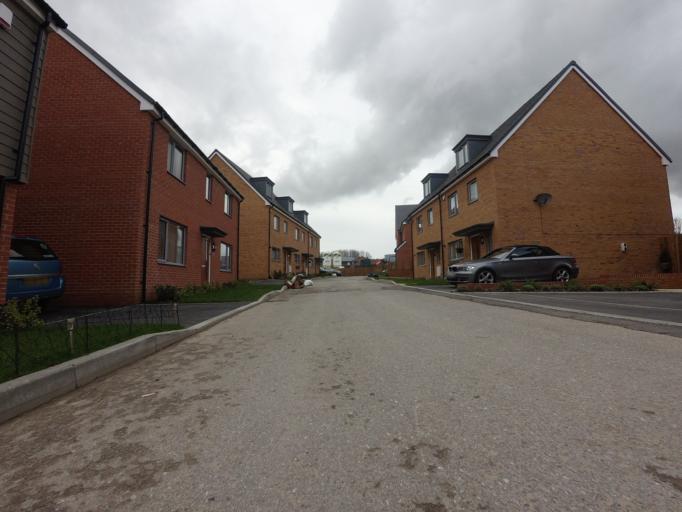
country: GB
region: England
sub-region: Kent
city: Swanley
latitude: 51.3921
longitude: 0.1768
